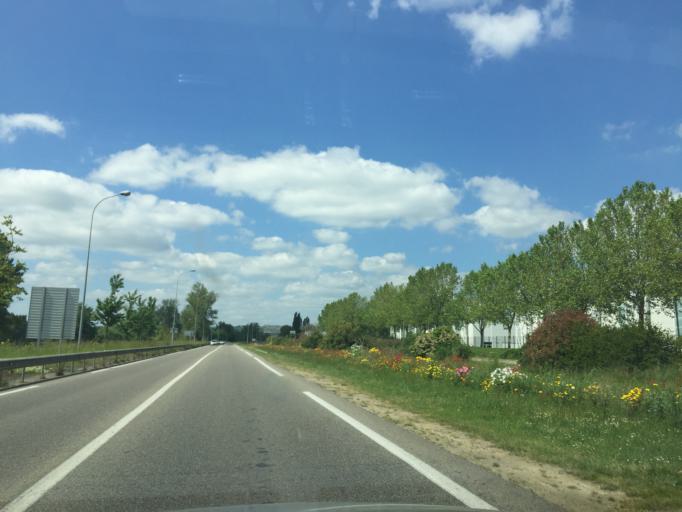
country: FR
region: Aquitaine
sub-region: Departement du Lot-et-Garonne
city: Boe
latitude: 44.1795
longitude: 0.6154
